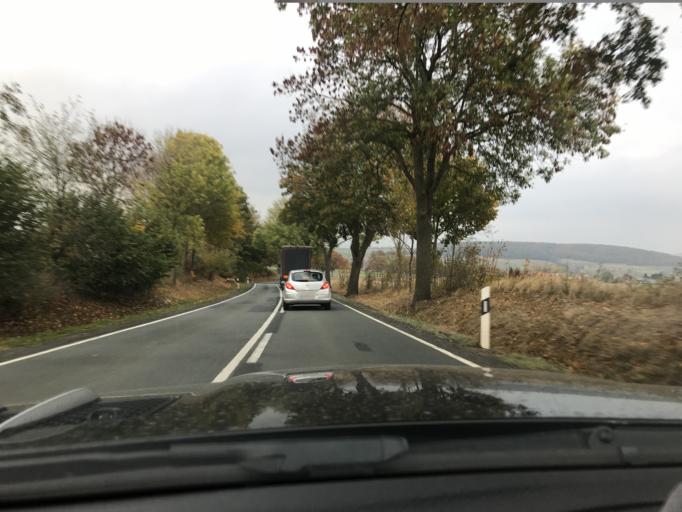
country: DE
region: Hesse
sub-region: Regierungsbezirk Kassel
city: Breuna
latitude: 51.4352
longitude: 9.2338
